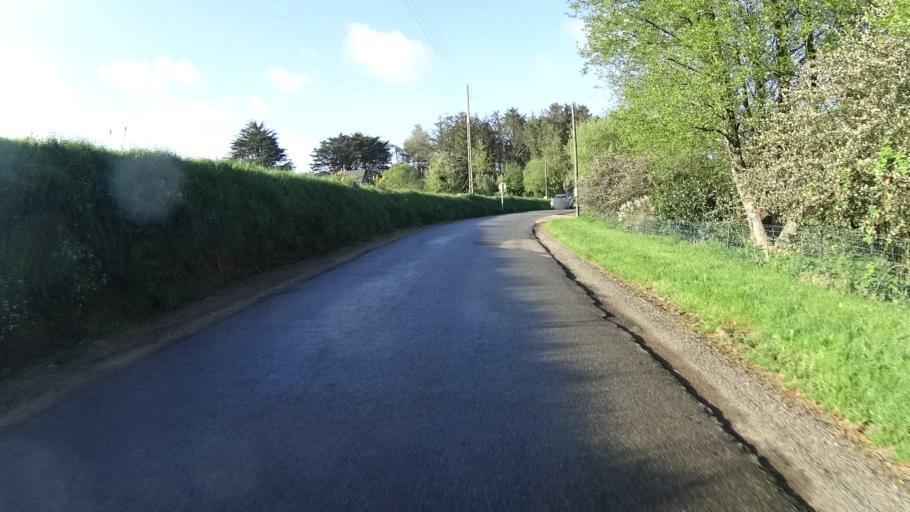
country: FR
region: Brittany
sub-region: Departement du Finistere
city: Ploumoguer
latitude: 48.4258
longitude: -4.7044
